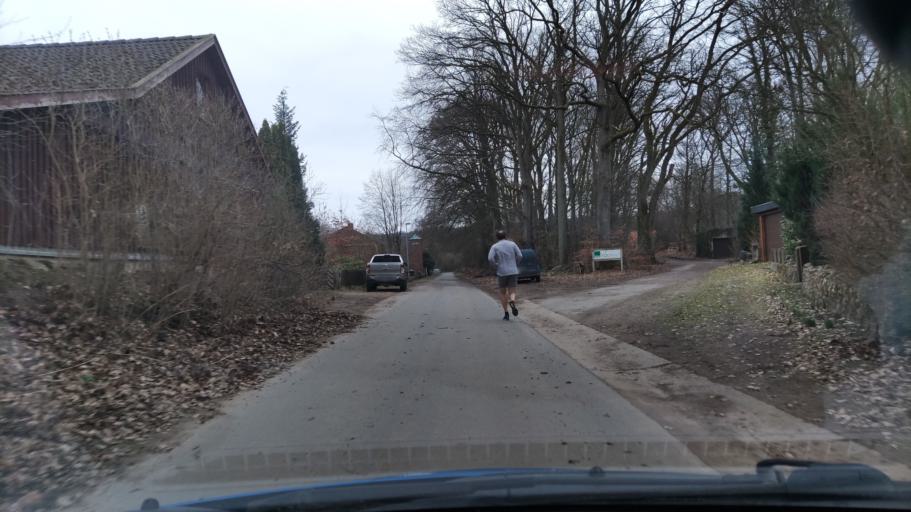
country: DE
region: Lower Saxony
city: Betzendorf
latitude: 53.1240
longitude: 10.3244
